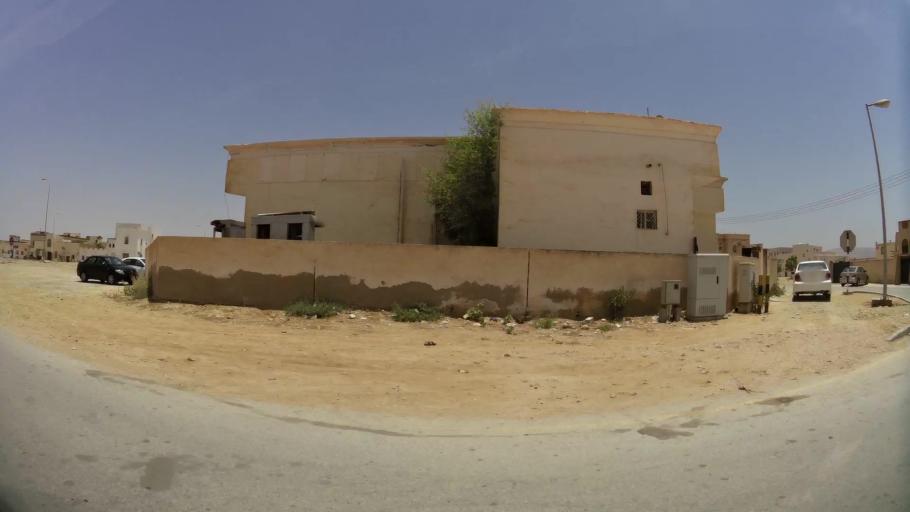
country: OM
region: Zufar
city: Salalah
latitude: 17.0830
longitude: 54.1542
